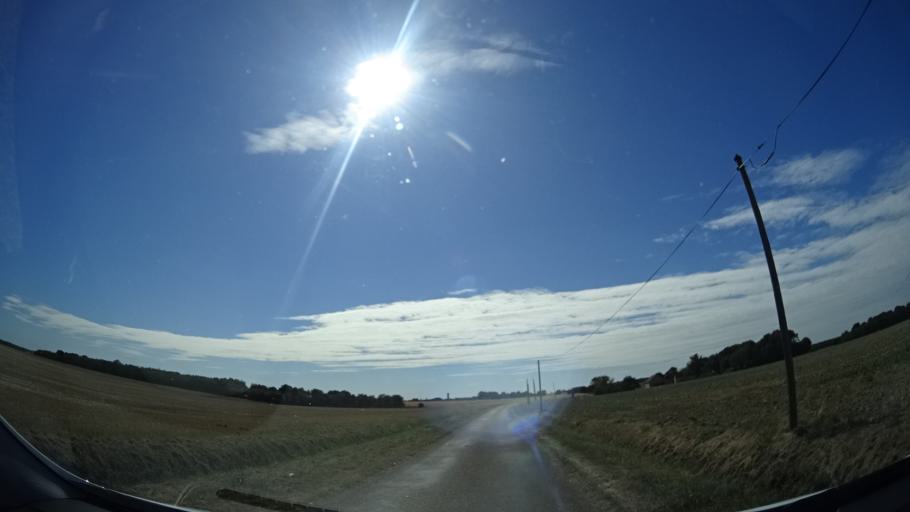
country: FR
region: Centre
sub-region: Departement du Loiret
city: Trigueres
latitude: 47.9471
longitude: 2.9583
